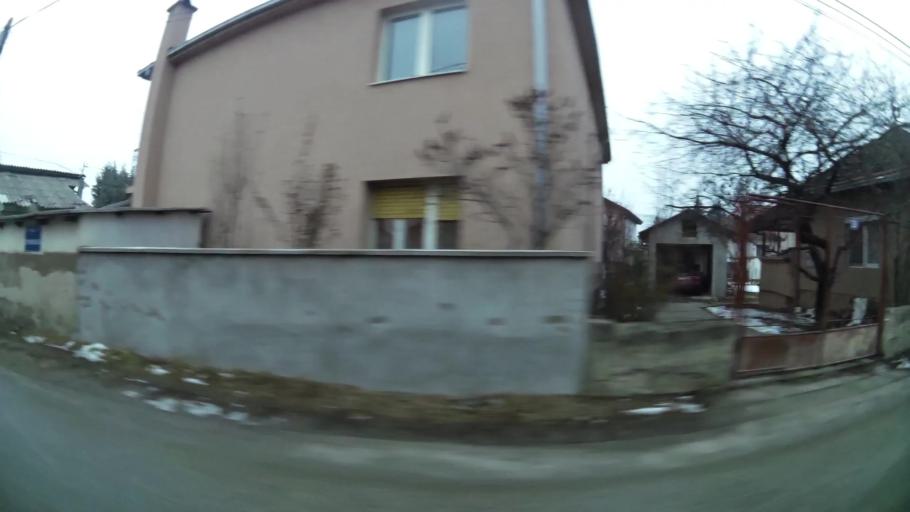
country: MK
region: Kisela Voda
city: Usje
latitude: 41.9701
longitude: 21.4820
